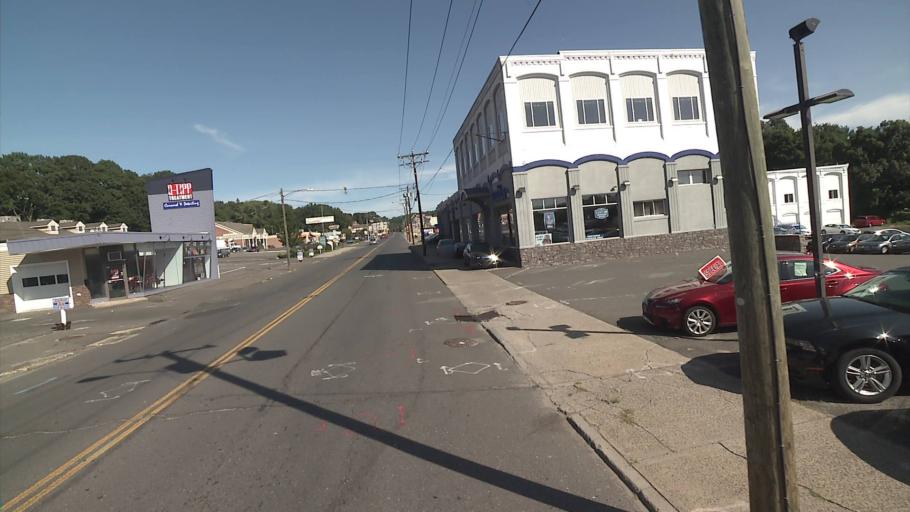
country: US
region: Connecticut
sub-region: New Haven County
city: Waterbury
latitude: 41.5655
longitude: -73.0596
